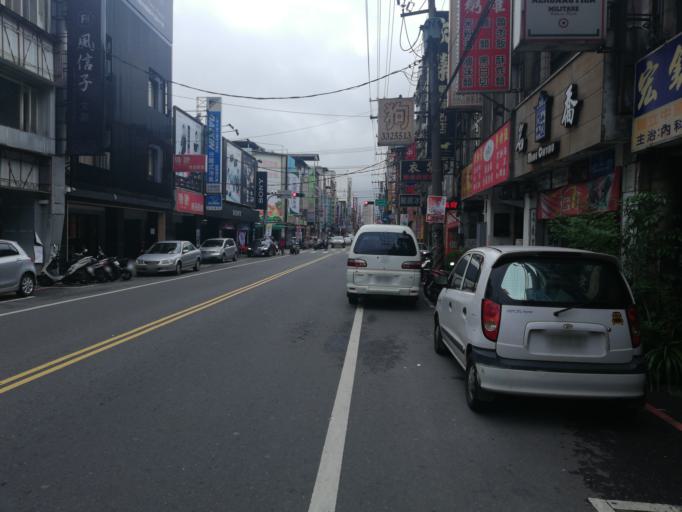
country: TW
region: Taiwan
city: Taoyuan City
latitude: 24.9997
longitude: 121.3078
